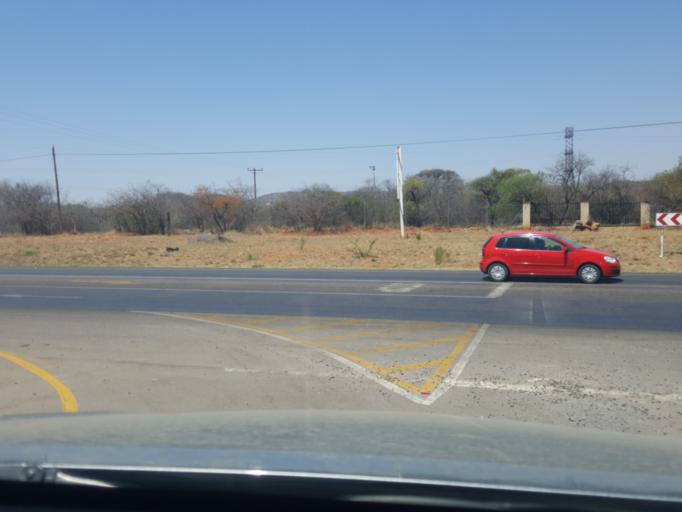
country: BW
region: South East
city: Lobatse
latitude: -25.1799
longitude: 25.6830
